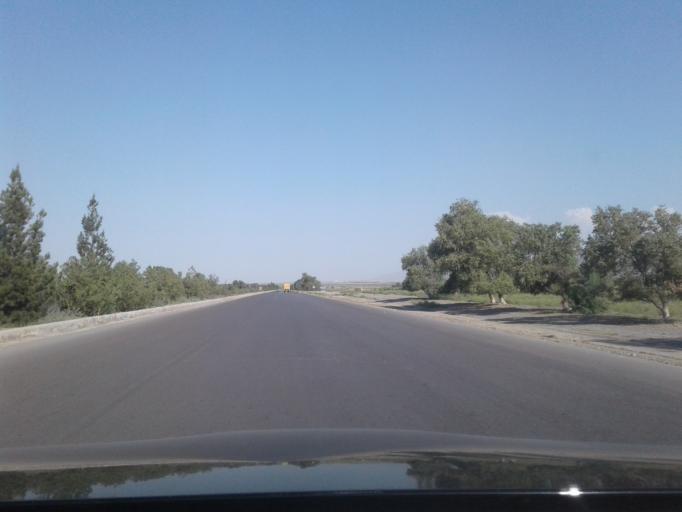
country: TM
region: Ahal
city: Arcabil
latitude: 38.1941
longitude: 57.8365
